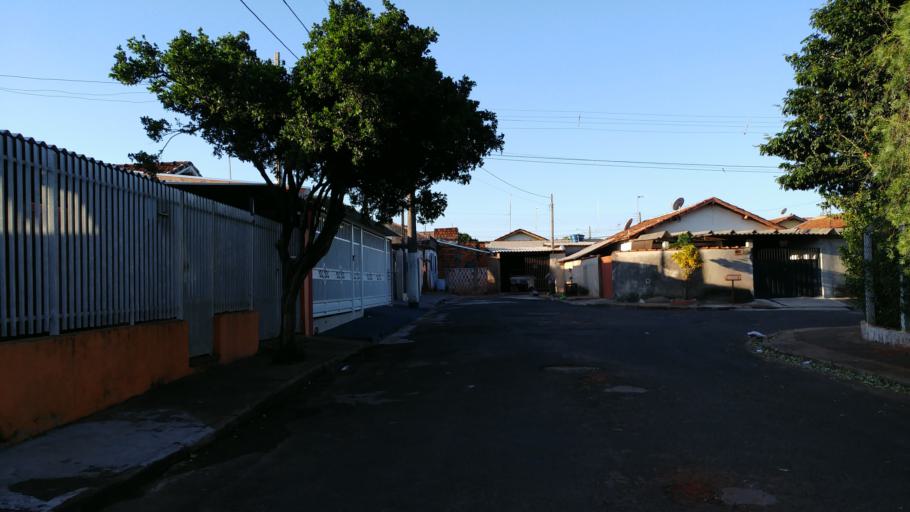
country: BR
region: Sao Paulo
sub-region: Paraguacu Paulista
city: Paraguacu Paulista
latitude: -22.4335
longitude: -50.5829
